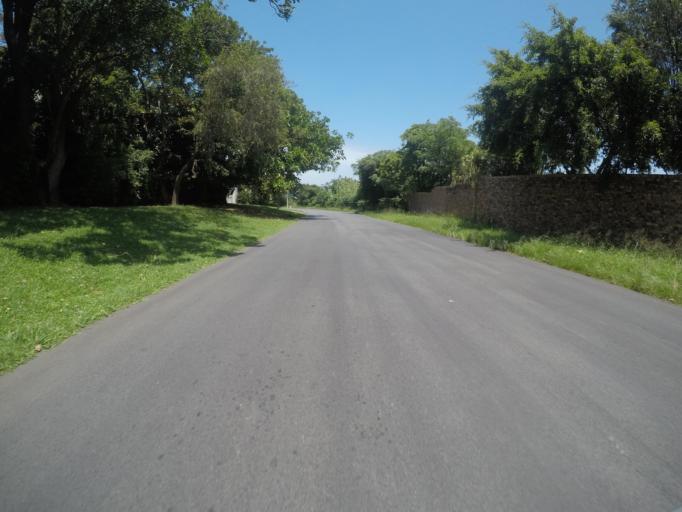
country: ZA
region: Eastern Cape
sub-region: Buffalo City Metropolitan Municipality
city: East London
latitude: -32.9990
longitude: 27.9243
